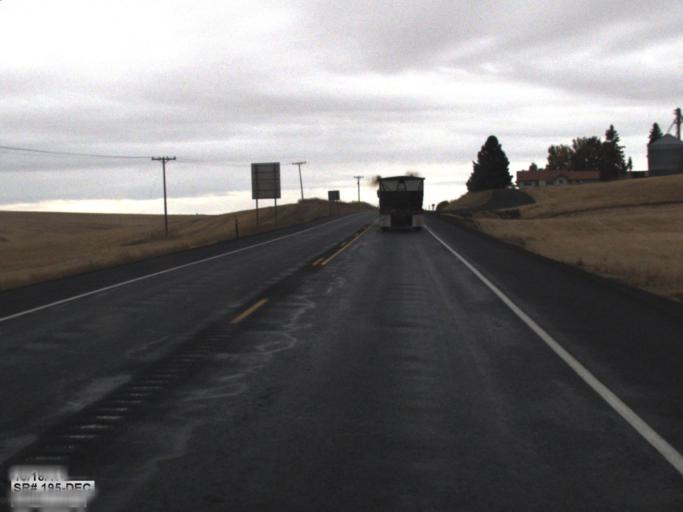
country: US
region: Washington
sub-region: Whitman County
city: Pullman
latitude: 46.7018
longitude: -117.2041
